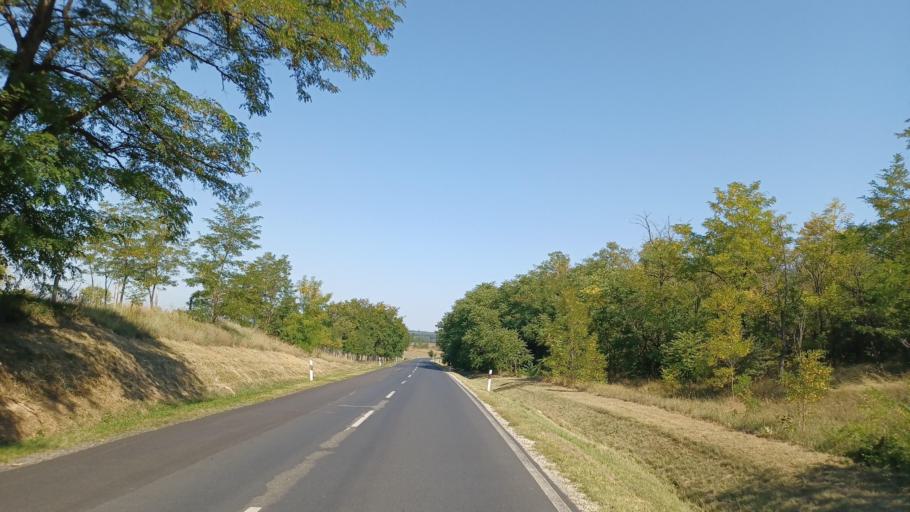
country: HU
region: Tolna
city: Nagydorog
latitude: 46.6580
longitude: 18.6529
